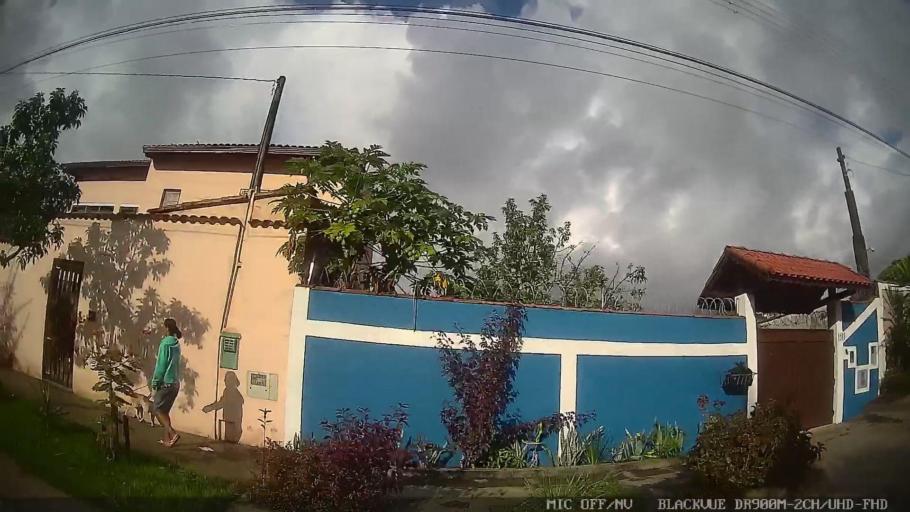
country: BR
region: Sao Paulo
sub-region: Itanhaem
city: Itanhaem
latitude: -24.1941
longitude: -46.8653
